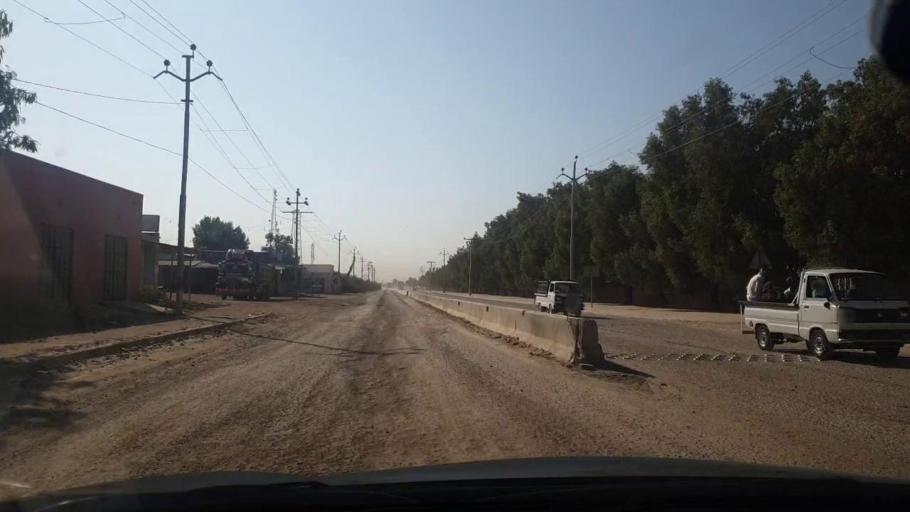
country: PK
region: Sindh
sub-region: Karachi District
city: Karachi
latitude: 25.0832
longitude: 67.0128
